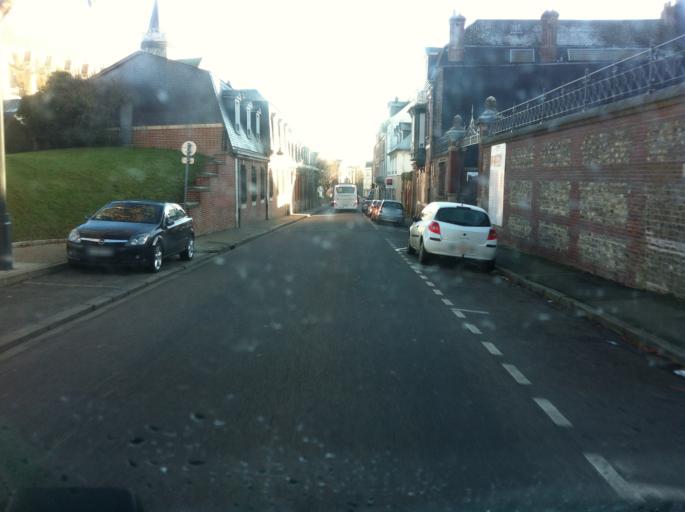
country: FR
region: Haute-Normandie
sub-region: Departement de la Seine-Maritime
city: Eu
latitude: 50.0485
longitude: 1.4176
